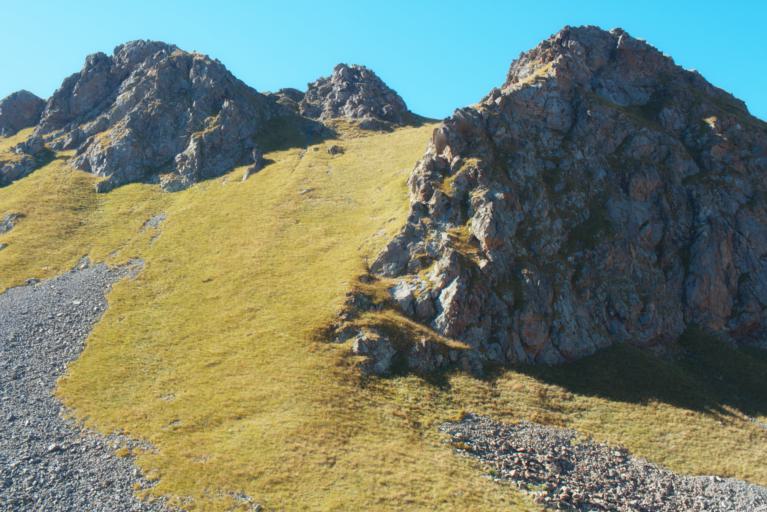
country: RU
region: Karachayevo-Cherkesiya
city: Mednogorskiy
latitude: 43.6111
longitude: 41.1391
